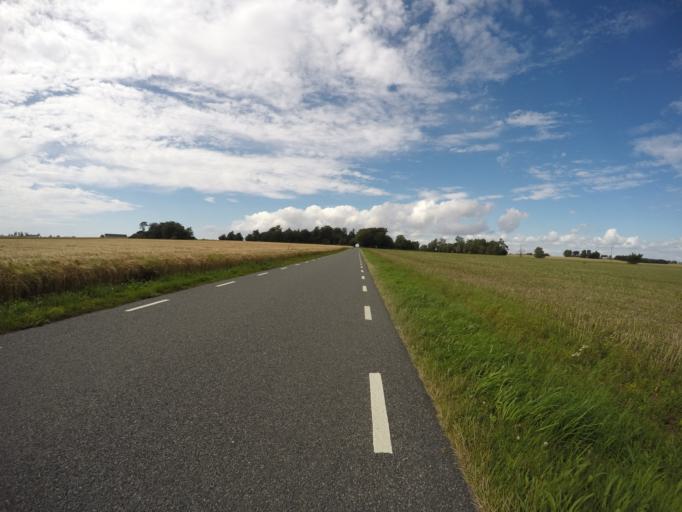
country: SE
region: Skane
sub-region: Simrishamns Kommun
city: Simrishamn
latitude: 55.4134
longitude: 14.1928
